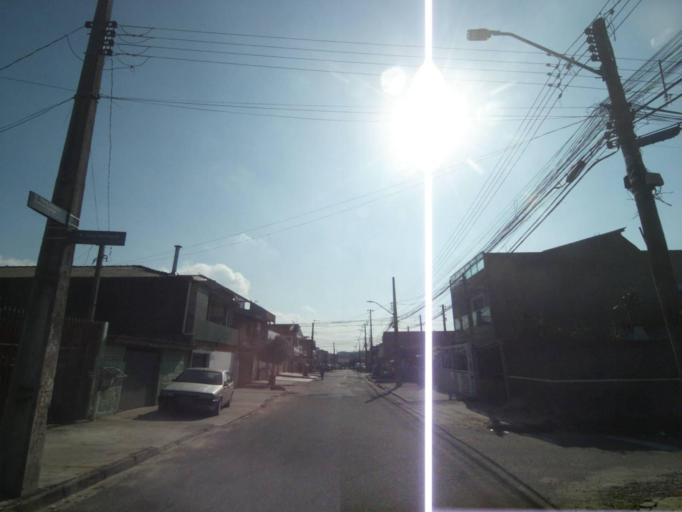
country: BR
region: Parana
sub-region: Araucaria
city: Araucaria
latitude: -25.5313
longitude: -49.3321
